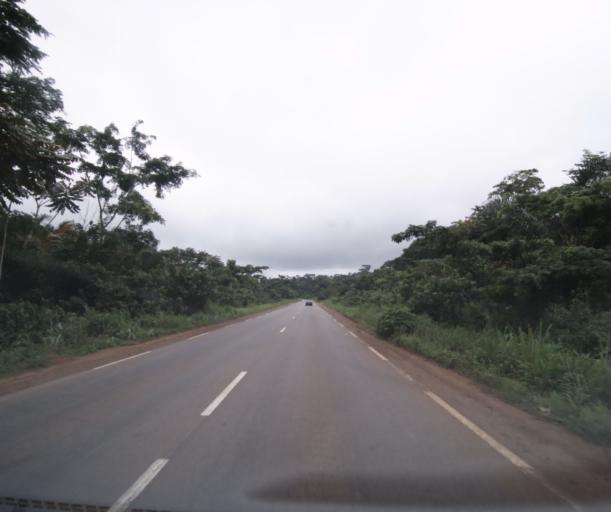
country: CM
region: Centre
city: Mbankomo
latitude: 3.7817
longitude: 11.2739
